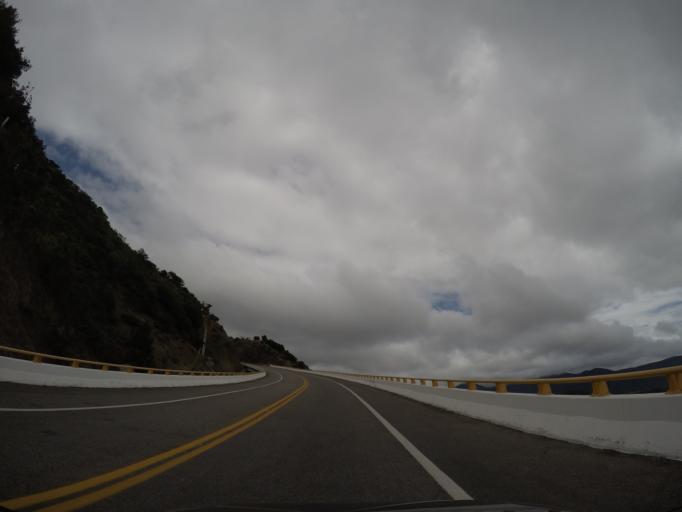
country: MX
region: Oaxaca
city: San Lorenzo Albarradas
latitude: 16.9351
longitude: -96.2663
